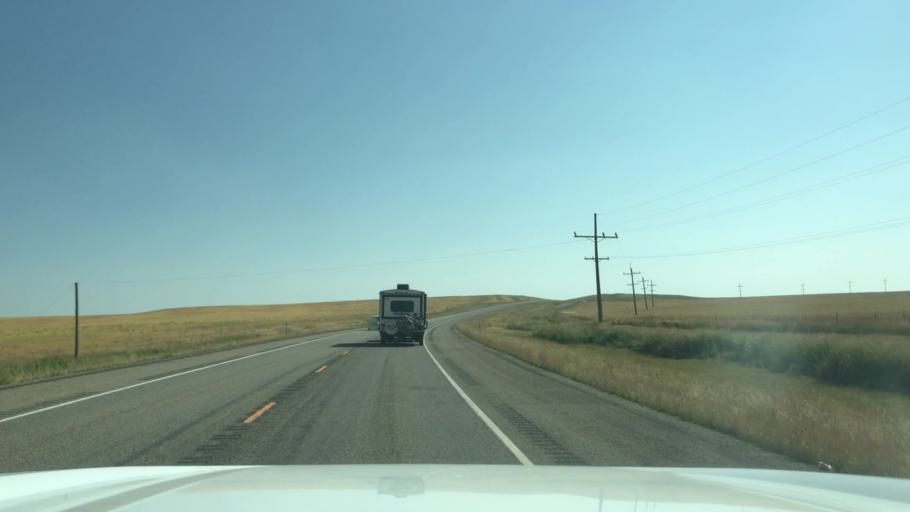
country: US
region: Montana
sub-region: Wheatland County
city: Harlowton
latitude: 46.4748
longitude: -109.7661
